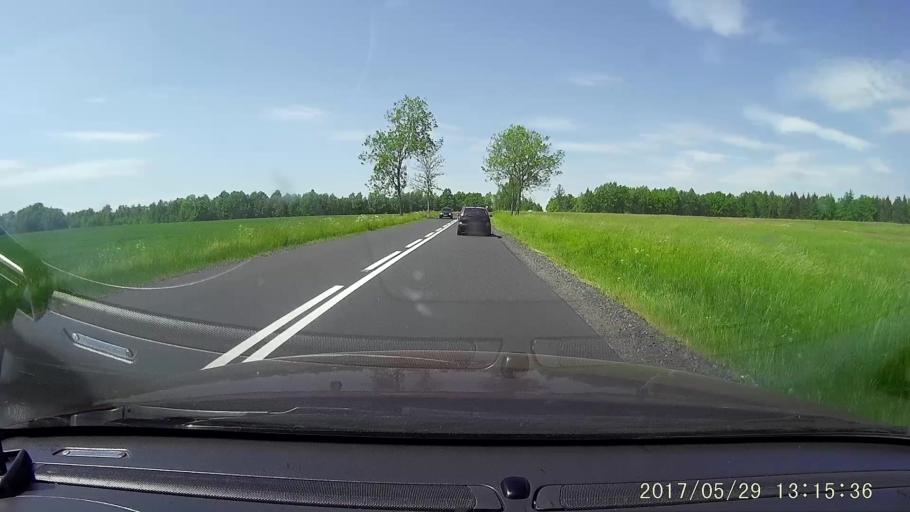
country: PL
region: Lower Silesian Voivodeship
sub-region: Powiat lwowecki
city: Lubomierz
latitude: 50.9883
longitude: 15.4808
